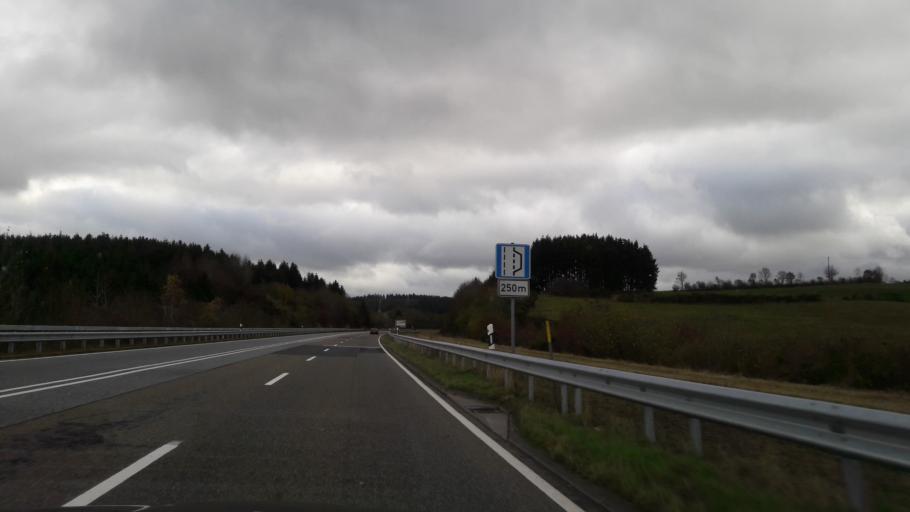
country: DE
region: Rheinland-Pfalz
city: Winterspelt
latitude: 50.2172
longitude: 6.2332
